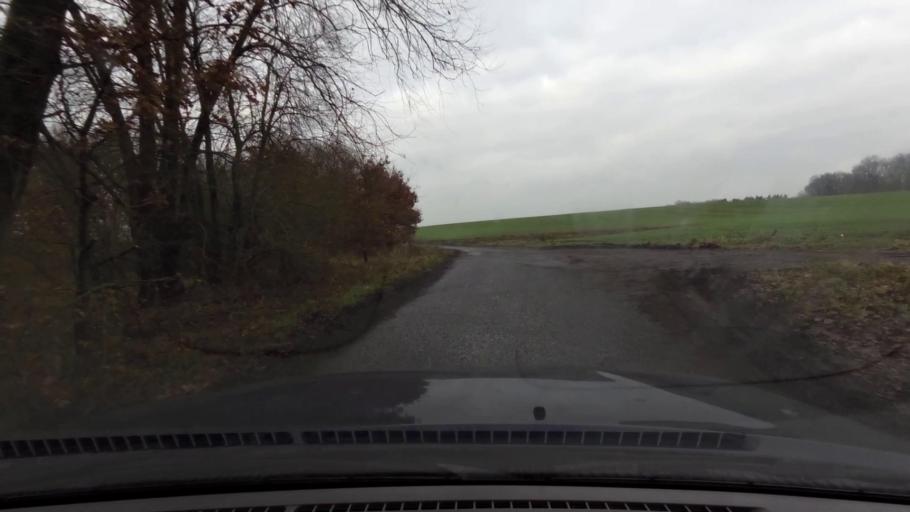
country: PL
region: West Pomeranian Voivodeship
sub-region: Powiat stargardzki
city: Stargard Szczecinski
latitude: 53.3330
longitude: 15.1298
